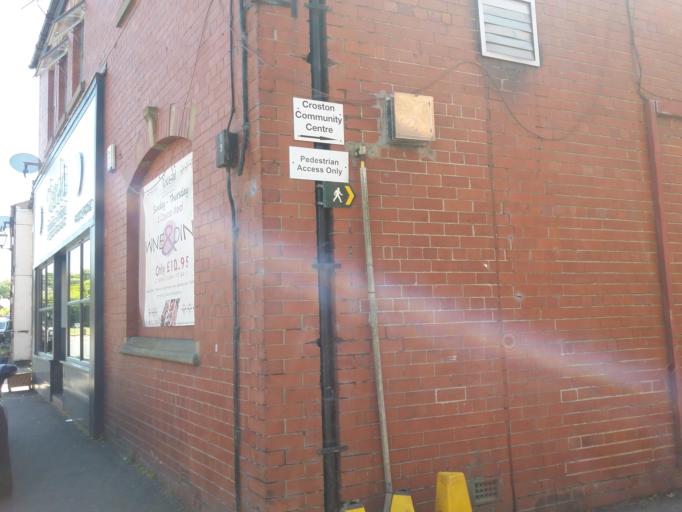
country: GB
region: England
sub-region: Lancashire
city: Croston
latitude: 53.6615
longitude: -2.7752
